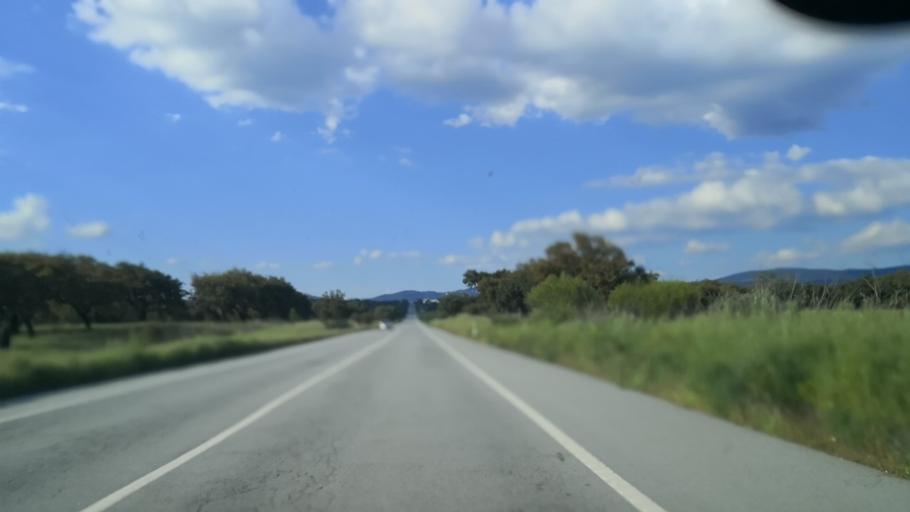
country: PT
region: Portalegre
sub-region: Portalegre
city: Urra
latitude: 39.2262
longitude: -7.4557
